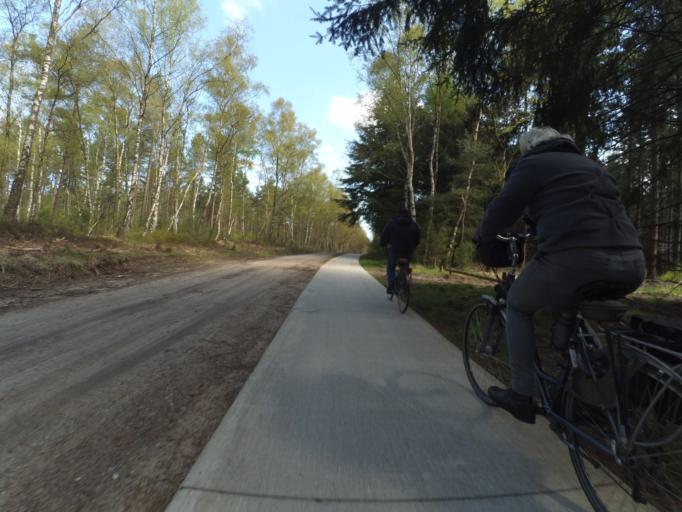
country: NL
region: Gelderland
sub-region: Gemeente Oldebroek
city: Oldebroek
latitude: 52.3681
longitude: 5.8981
